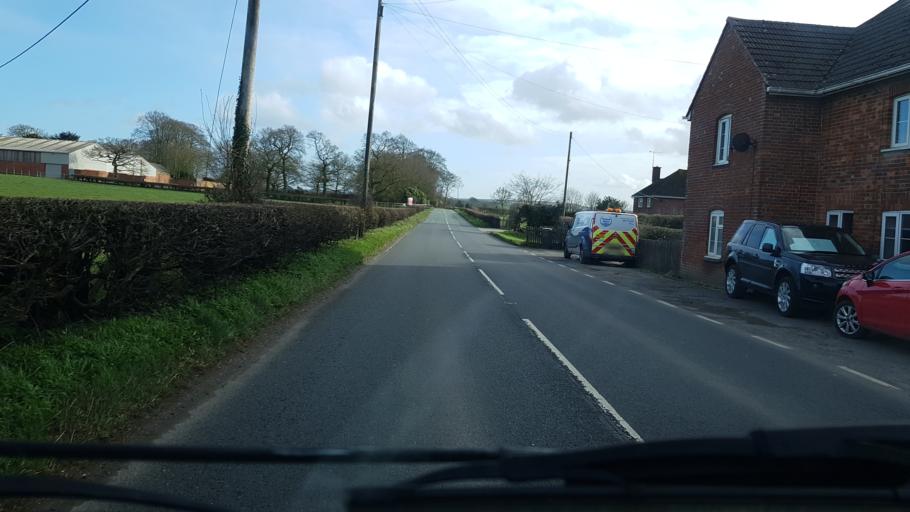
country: GB
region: England
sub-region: Wiltshire
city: Avebury
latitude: 51.4424
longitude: -1.8565
